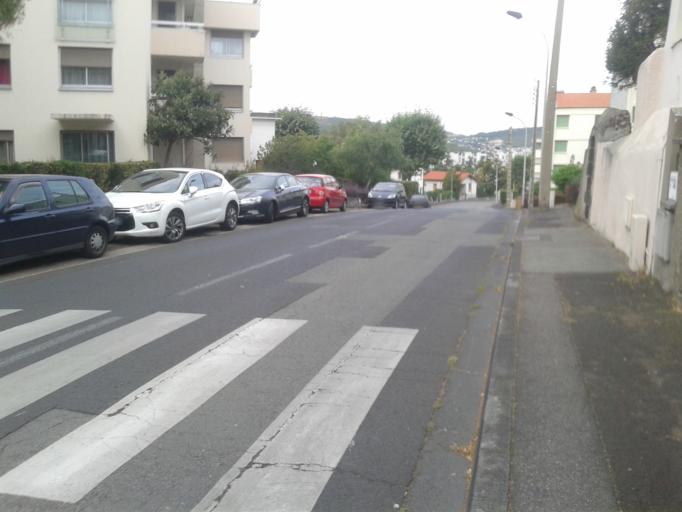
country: FR
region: Auvergne
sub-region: Departement du Puy-de-Dome
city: Chamalieres
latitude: 45.7710
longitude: 3.0651
